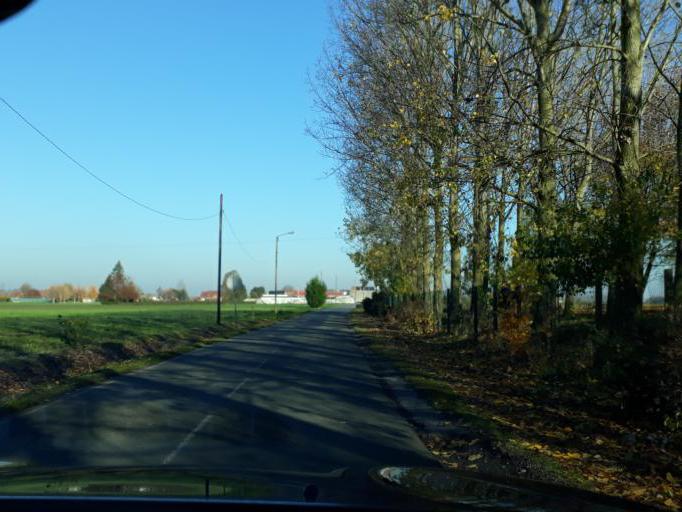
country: FR
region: Nord-Pas-de-Calais
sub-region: Departement du Nord
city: Masny
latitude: 50.3394
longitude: 3.2056
